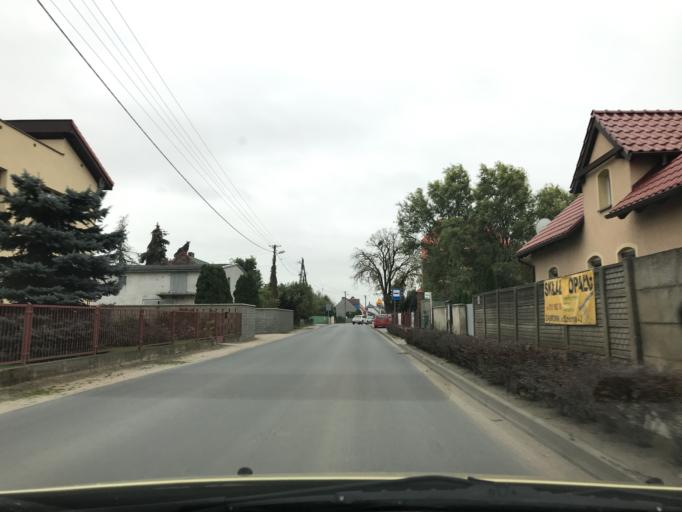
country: PL
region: Greater Poland Voivodeship
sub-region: Powiat poznanski
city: Baranowo
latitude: 52.4041
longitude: 16.7394
